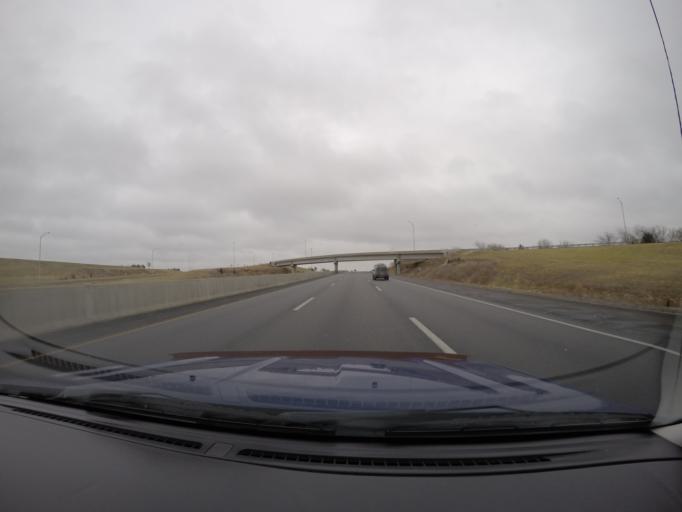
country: US
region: Kansas
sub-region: Shawnee County
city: Topeka
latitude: 39.0183
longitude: -95.5145
